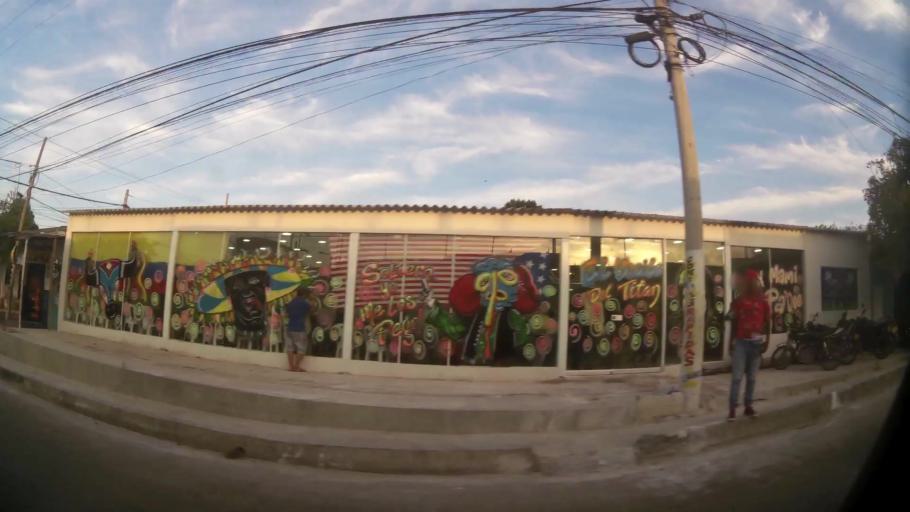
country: CO
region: Atlantico
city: Barranquilla
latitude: 10.9548
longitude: -74.8211
